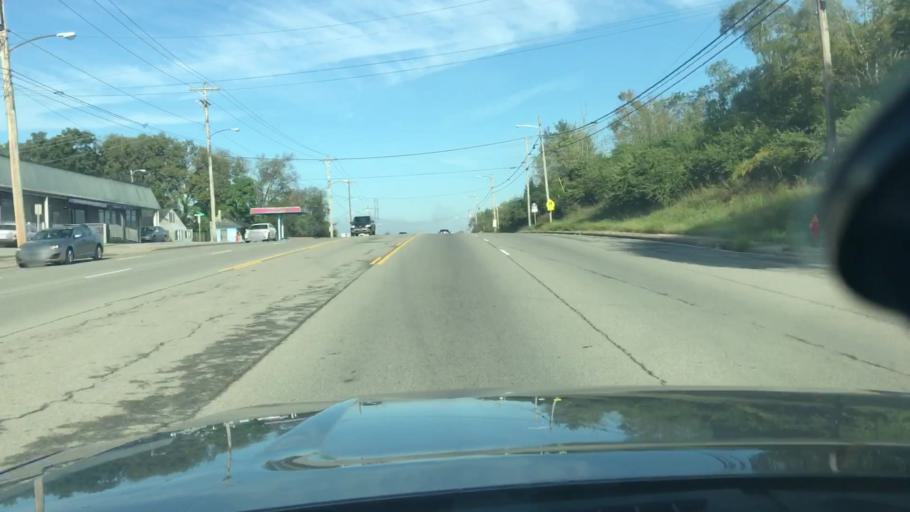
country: US
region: Tennessee
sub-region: Davidson County
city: Nashville
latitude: 36.1949
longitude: -86.8331
